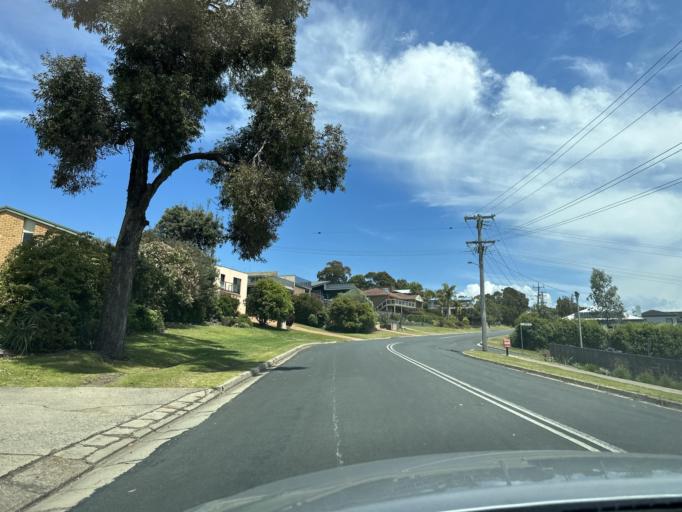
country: AU
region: New South Wales
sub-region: Bega Valley
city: Merimbula
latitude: -36.8915
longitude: 149.9061
